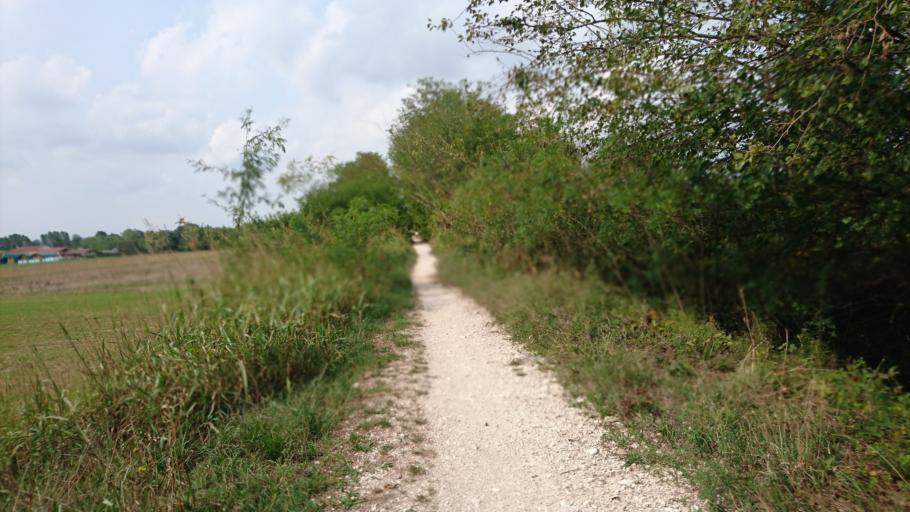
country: IT
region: Veneto
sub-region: Provincia di Padova
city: Saletto
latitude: 45.4690
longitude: 11.8607
